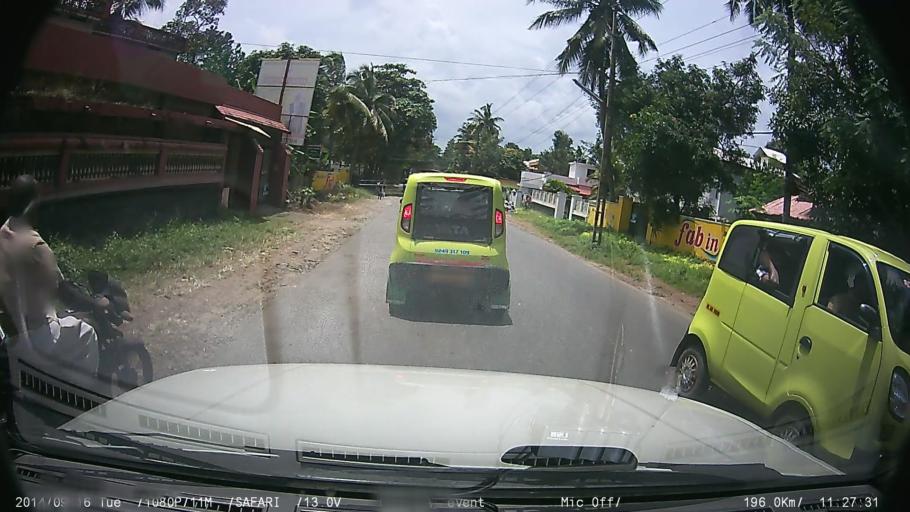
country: IN
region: Kerala
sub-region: Kottayam
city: Changanacheri
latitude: 9.4768
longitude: 76.5280
